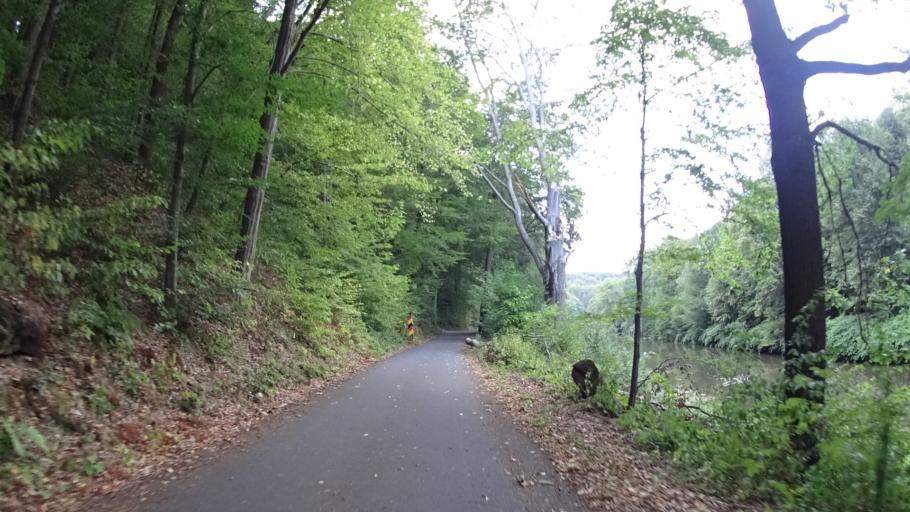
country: DE
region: Saxony
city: Ostritz
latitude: 50.9899
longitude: 14.9172
